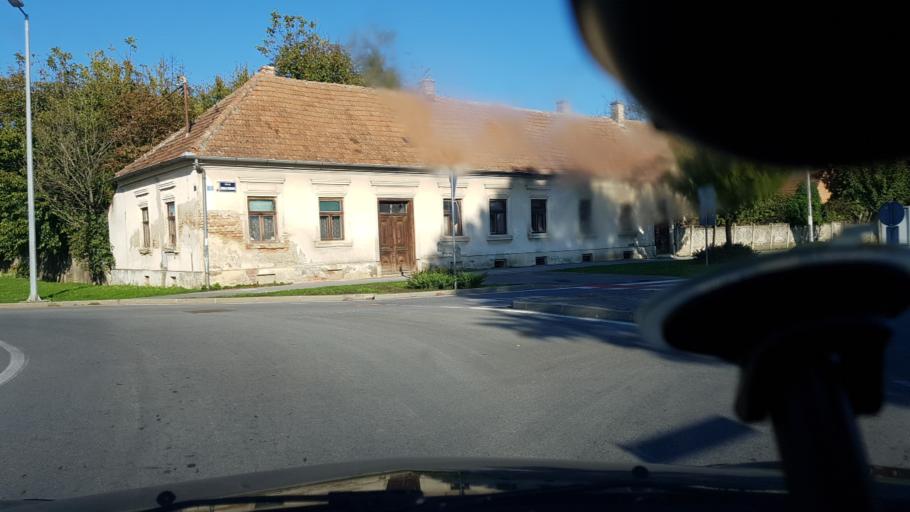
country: HR
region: Bjelovarsko-Bilogorska
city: Bjelovar
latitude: 45.9099
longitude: 16.8523
